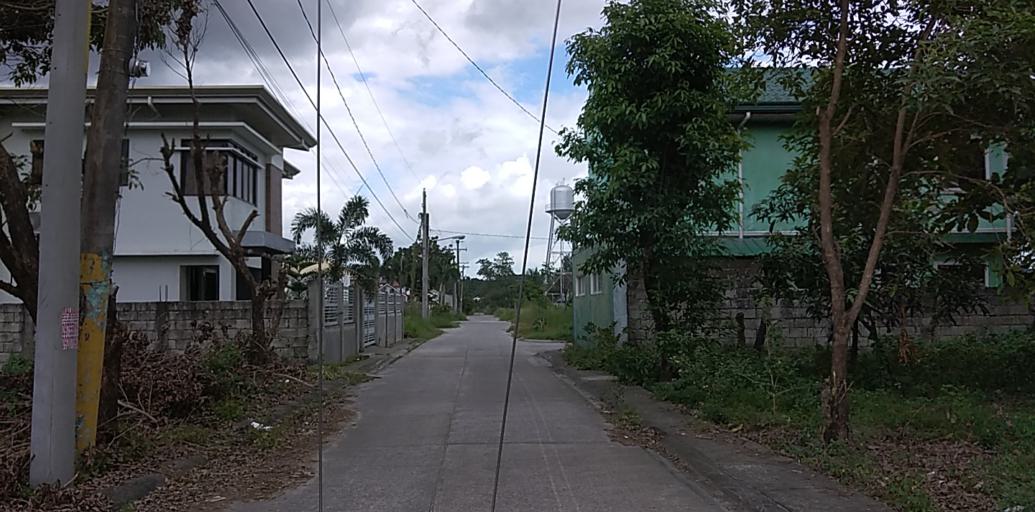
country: PH
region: Central Luzon
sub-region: Province of Pampanga
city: Porac
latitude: 15.0639
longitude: 120.5455
